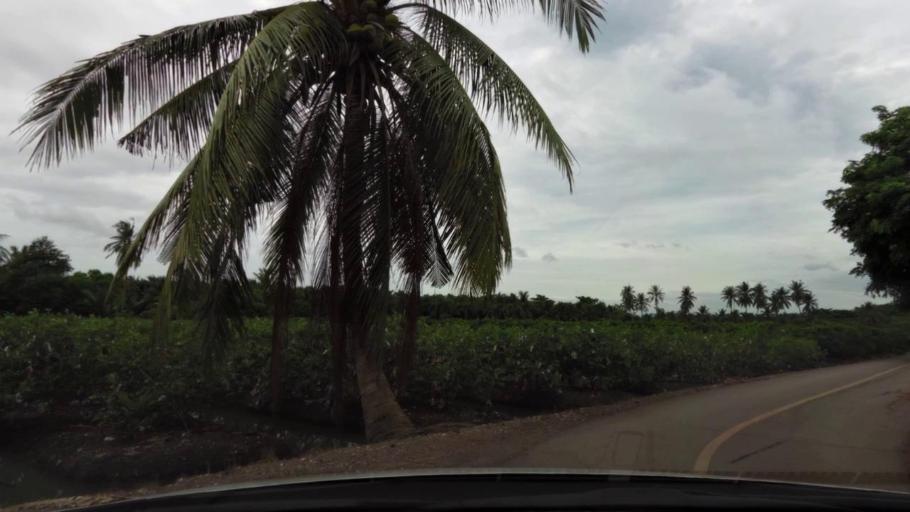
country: TH
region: Ratchaburi
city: Damnoen Saduak
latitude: 13.5537
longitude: 99.9733
